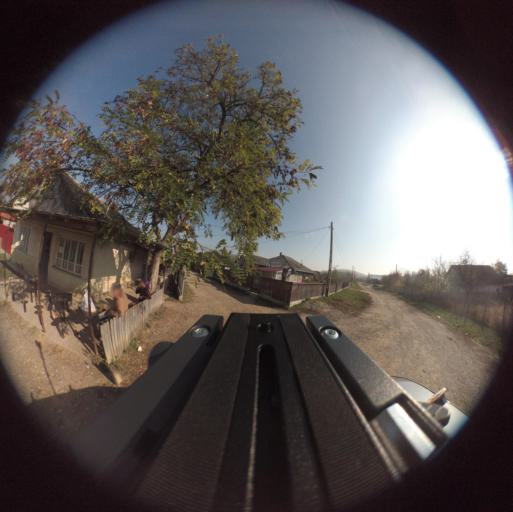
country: RO
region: Vaslui
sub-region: Comuna Dumesti
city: Dumesti
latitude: 46.8321
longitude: 27.2643
